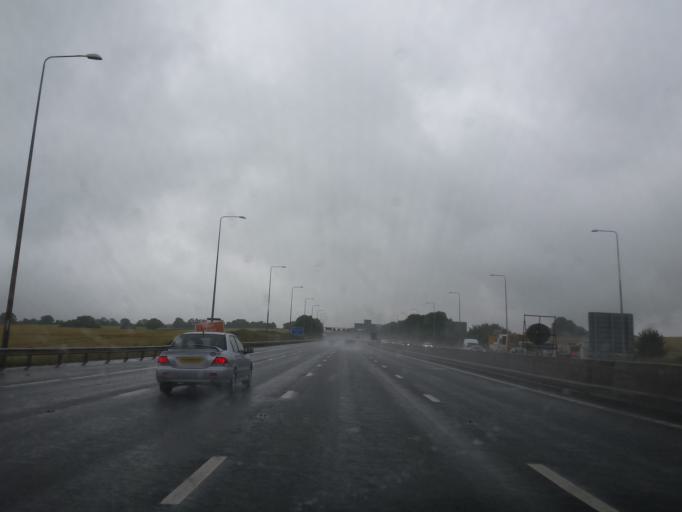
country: GB
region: England
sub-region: Derbyshire
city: Pinxton
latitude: 53.0871
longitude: -1.3021
